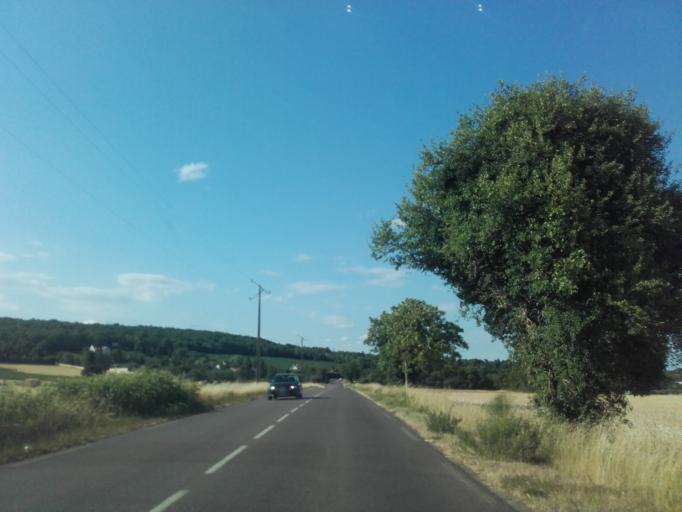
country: FR
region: Bourgogne
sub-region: Departement de Saone-et-Loire
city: Fontaines
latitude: 46.8411
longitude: 4.7523
